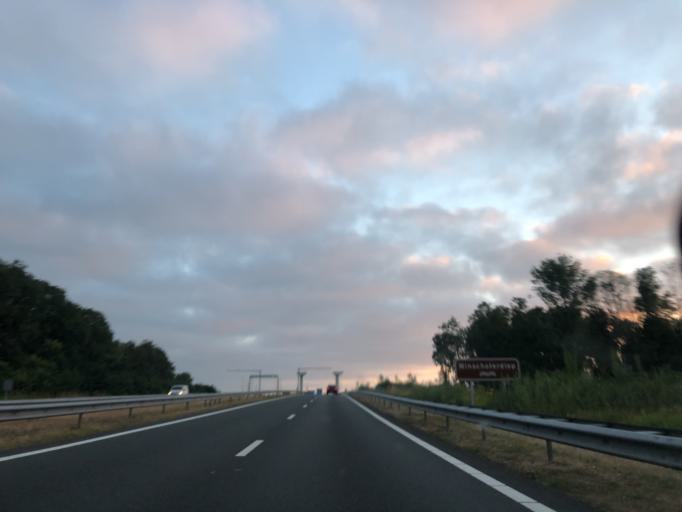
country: NL
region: Groningen
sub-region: Gemeente Veendam
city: Veendam
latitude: 53.1613
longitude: 6.8955
